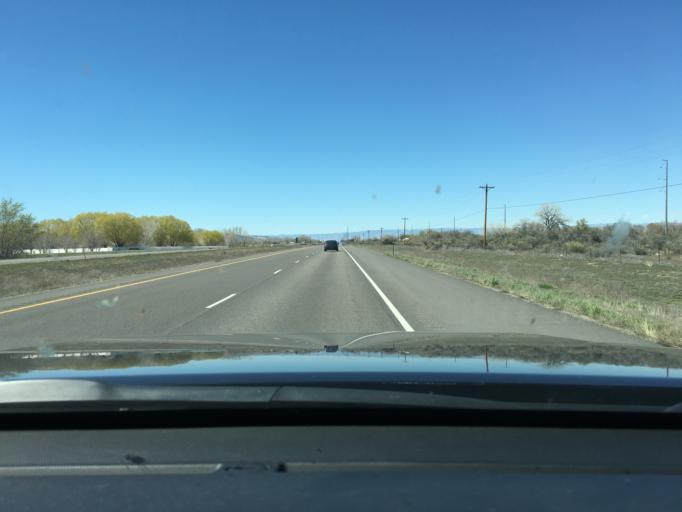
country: US
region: Colorado
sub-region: Mesa County
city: Fruita
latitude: 39.1333
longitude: -108.6921
